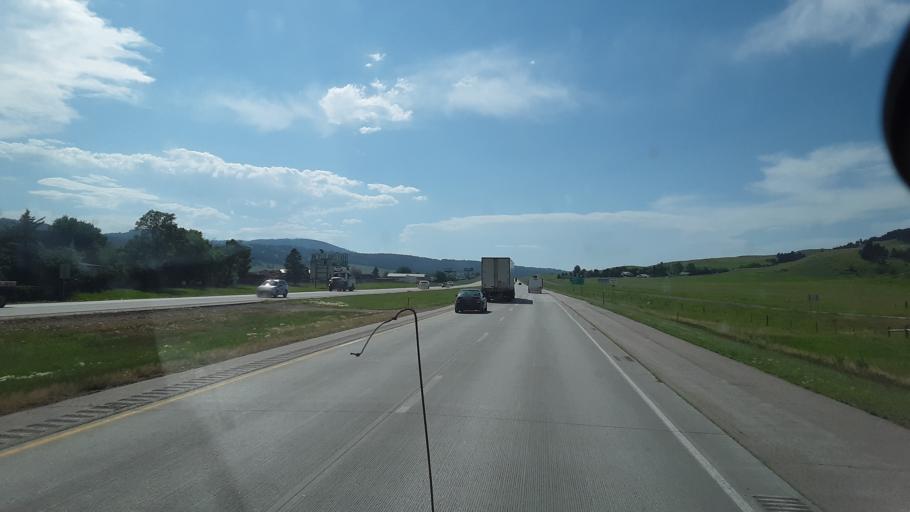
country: US
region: South Dakota
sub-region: Meade County
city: Sturgis
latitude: 44.4224
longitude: -103.5434
